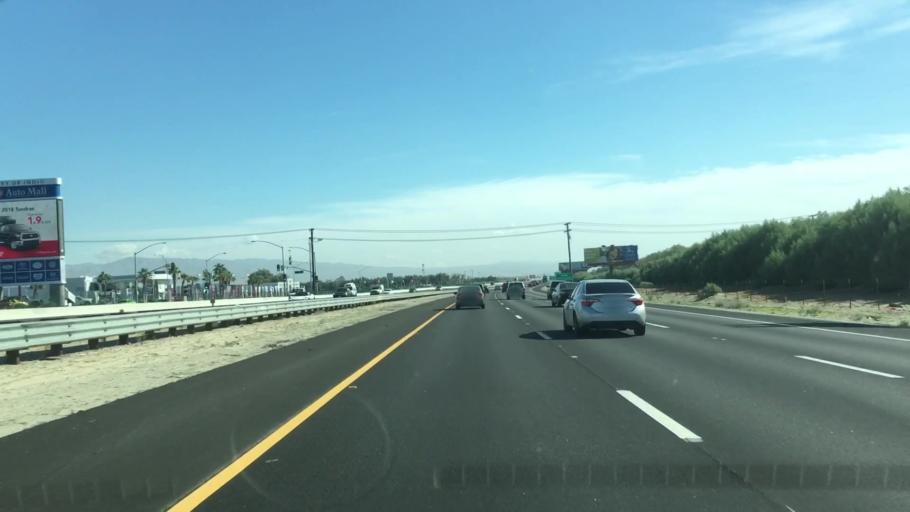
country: US
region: California
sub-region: Riverside County
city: Bermuda Dunes
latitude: 33.7558
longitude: -116.2883
